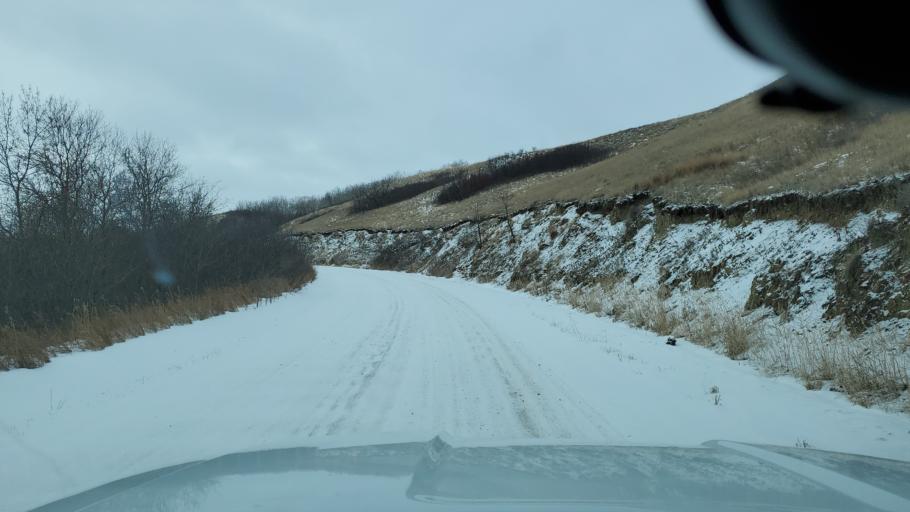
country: CA
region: Saskatchewan
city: White City
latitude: 50.7719
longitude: -104.1458
